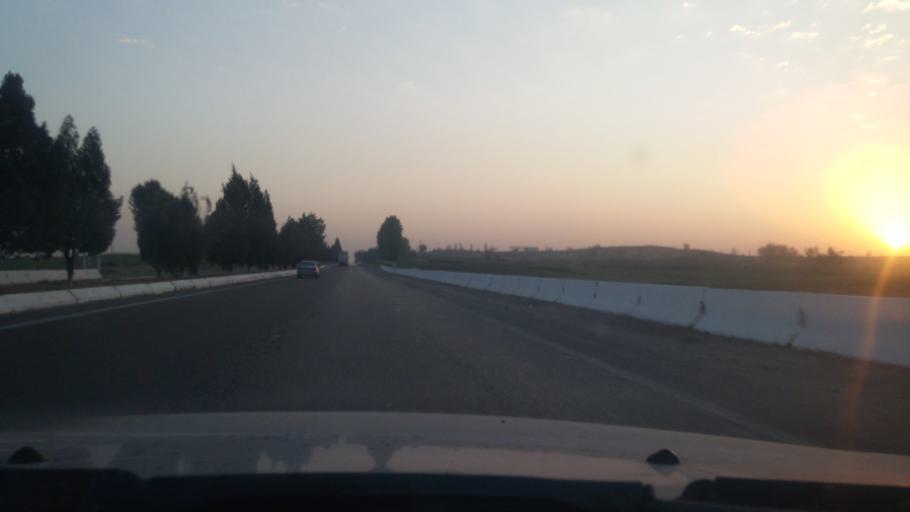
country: UZ
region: Toshkent
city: Amir Timur
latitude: 41.0428
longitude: 68.8845
